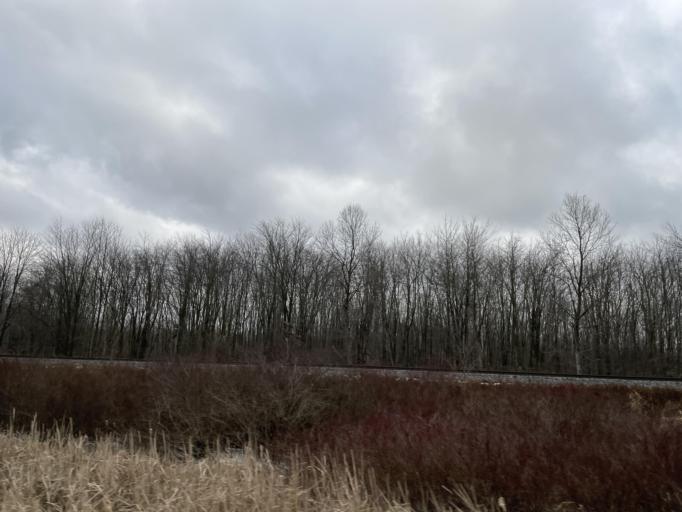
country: CA
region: Ontario
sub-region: Wellington County
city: Guelph
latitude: 43.5082
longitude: -80.3374
